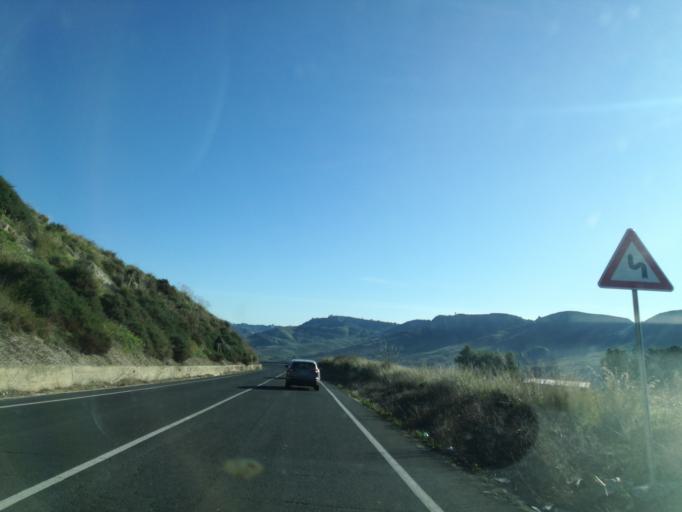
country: IT
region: Sicily
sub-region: Catania
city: San Michele di Ganzaria
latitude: 37.2303
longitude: 14.4428
